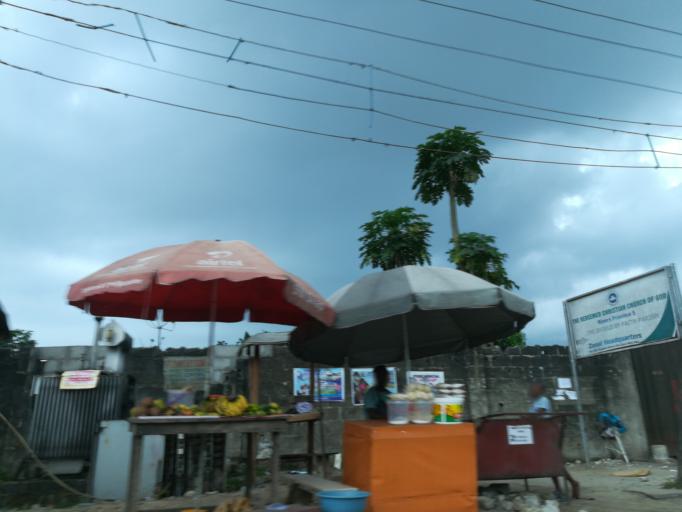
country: NG
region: Rivers
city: Port Harcourt
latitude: 4.8173
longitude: 7.0673
